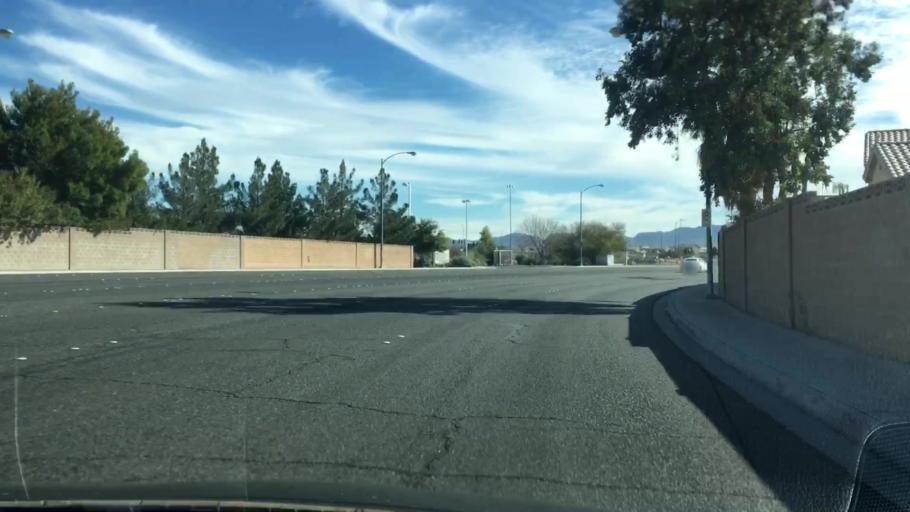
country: US
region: Nevada
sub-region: Clark County
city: Paradise
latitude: 36.0442
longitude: -115.1369
